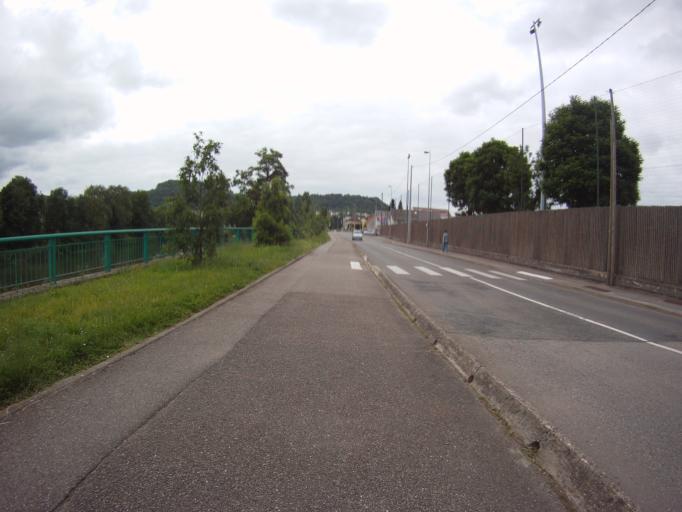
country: FR
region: Lorraine
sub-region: Departement de Meurthe-et-Moselle
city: Malzeville
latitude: 48.7116
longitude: 6.1784
